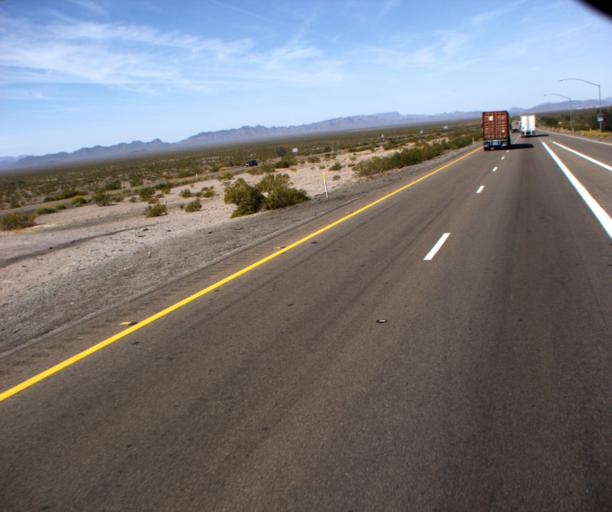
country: US
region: Arizona
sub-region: La Paz County
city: Salome
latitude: 33.6139
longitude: -113.6504
